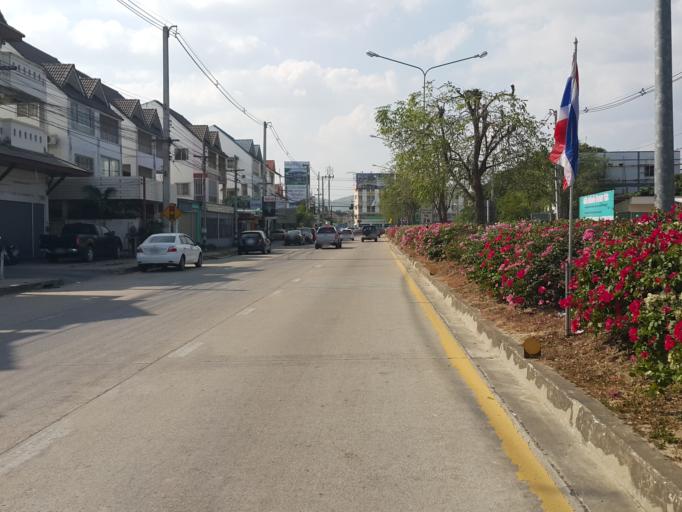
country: TH
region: Chiang Mai
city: Chiang Mai
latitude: 18.7491
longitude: 98.9429
